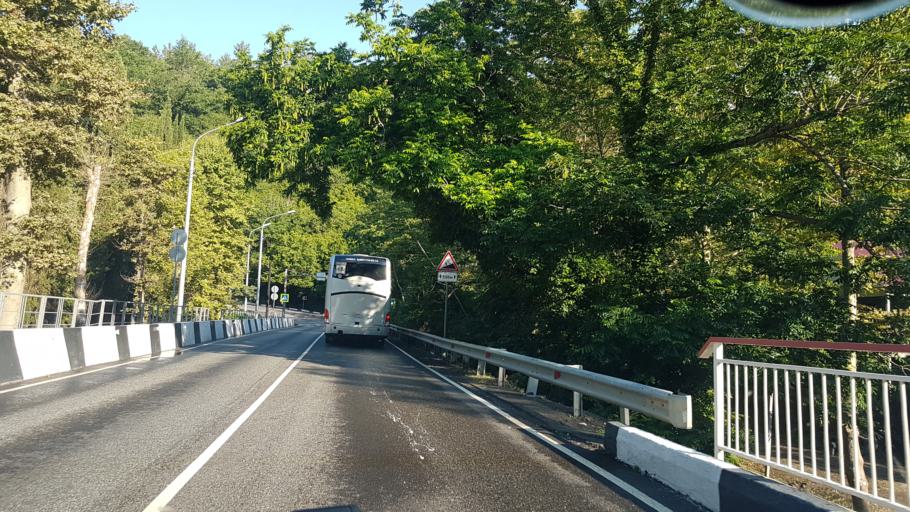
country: RU
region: Krasnodarskiy
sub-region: Sochi City
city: Lazarevskoye
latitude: 43.8541
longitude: 39.4107
